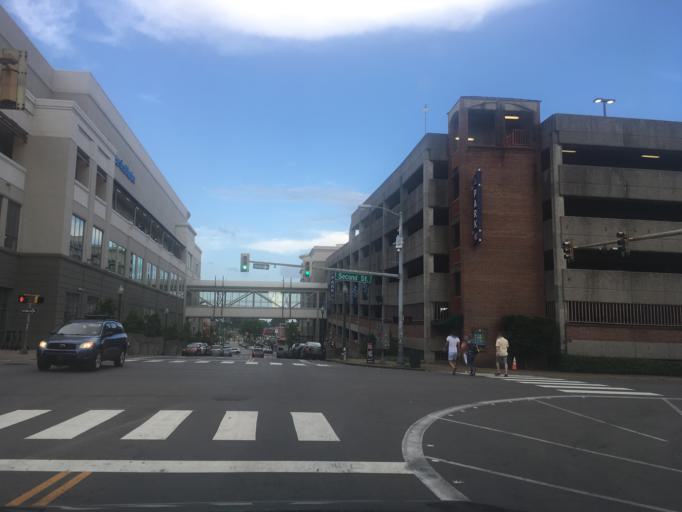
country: US
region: Tennessee
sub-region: Shelby County
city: Memphis
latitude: 35.1407
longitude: -90.0534
